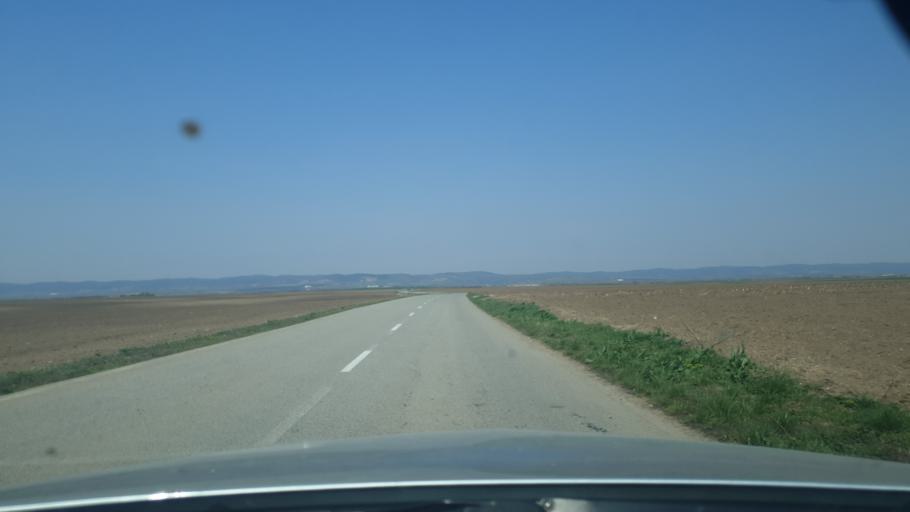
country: RS
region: Autonomna Pokrajina Vojvodina
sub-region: Sremski Okrug
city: Ruma
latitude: 45.0313
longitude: 19.7622
